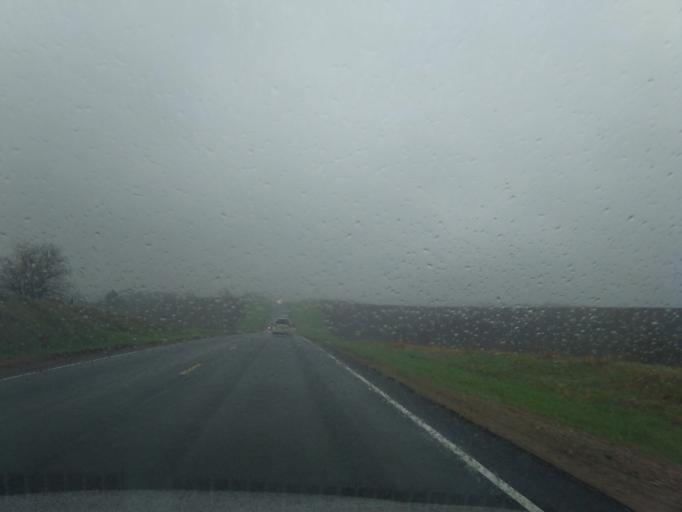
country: US
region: Nebraska
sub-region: Wayne County
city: Wayne
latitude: 42.1854
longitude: -97.1788
